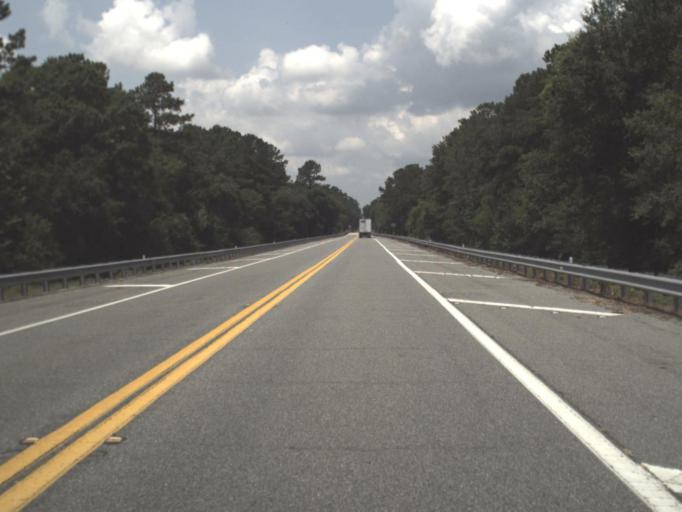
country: US
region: Florida
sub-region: Madison County
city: Madison
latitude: 30.4836
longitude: -83.2402
